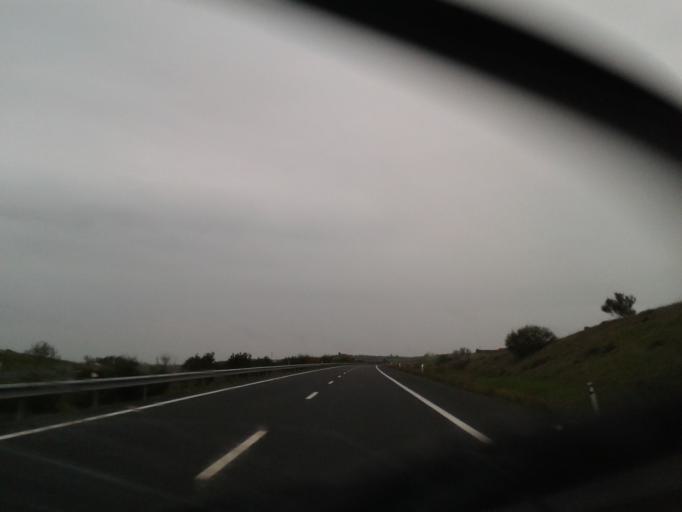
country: PT
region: Beja
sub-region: Aljustrel
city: Aljustrel
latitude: 37.8116
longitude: -8.2297
